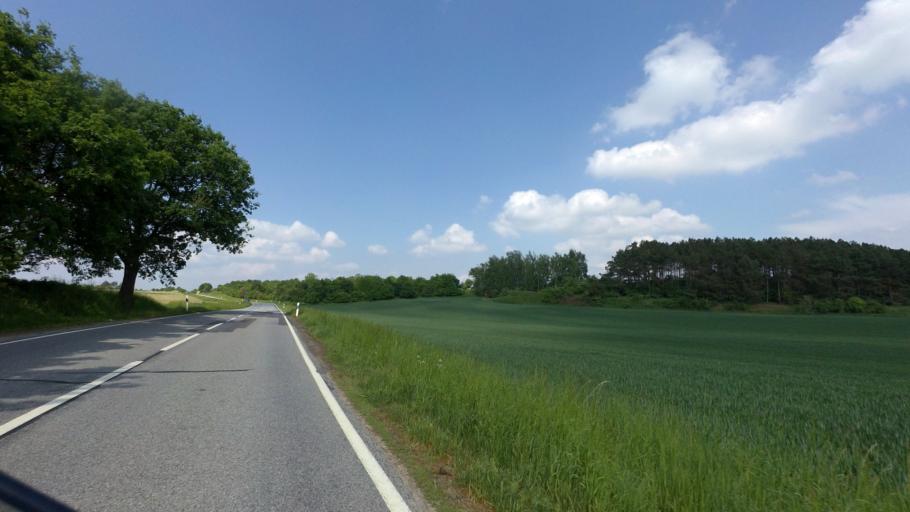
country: DE
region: Saxony
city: Weissenberg
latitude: 51.2033
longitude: 14.6044
